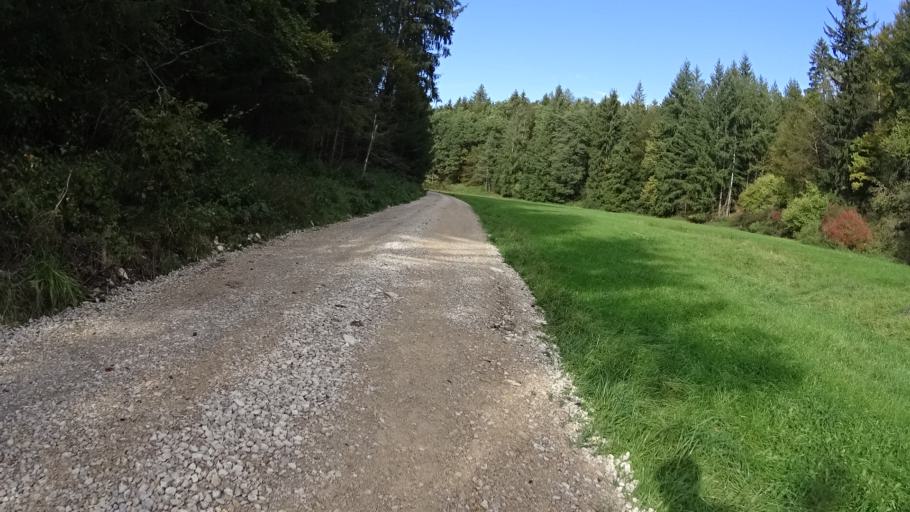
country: DE
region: Bavaria
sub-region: Upper Bavaria
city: Bohmfeld
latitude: 48.8881
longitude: 11.3573
